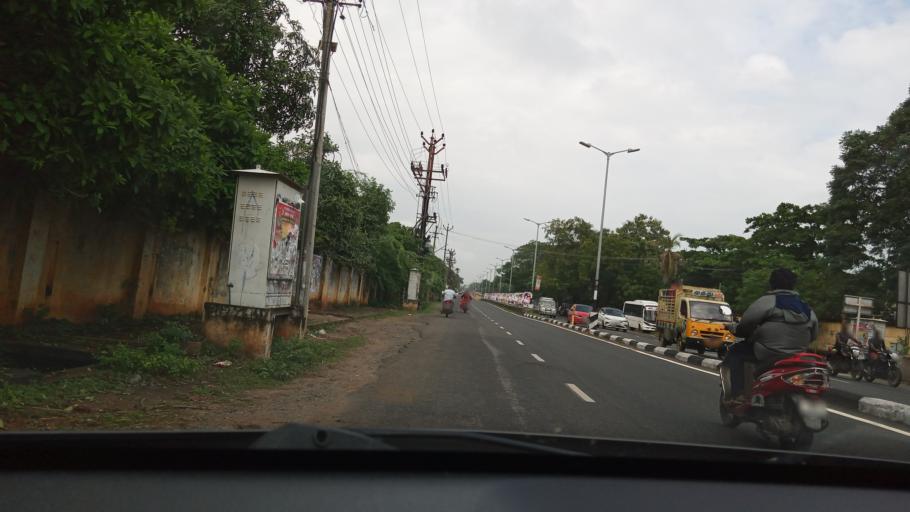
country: IN
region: Tamil Nadu
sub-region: Villupuram
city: Auroville
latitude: 12.0092
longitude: 79.8563
